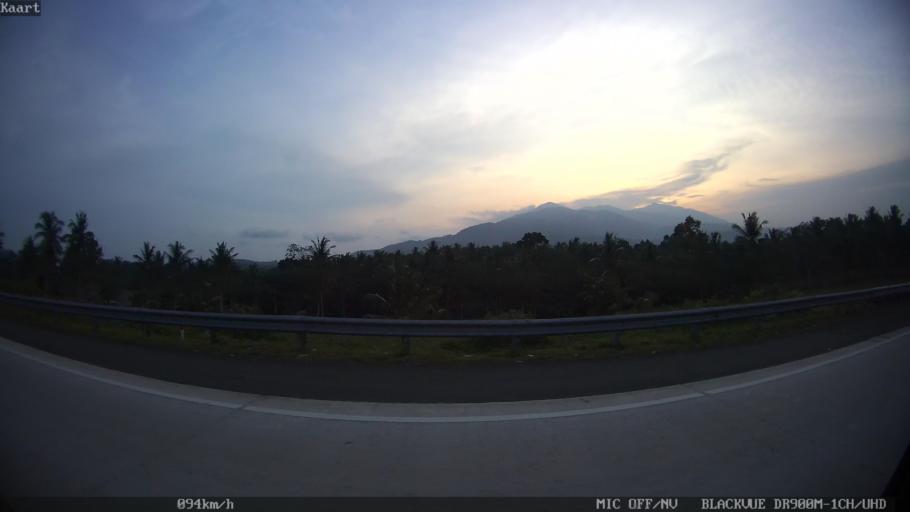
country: ID
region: Lampung
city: Penengahan
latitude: -5.7817
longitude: 105.7216
